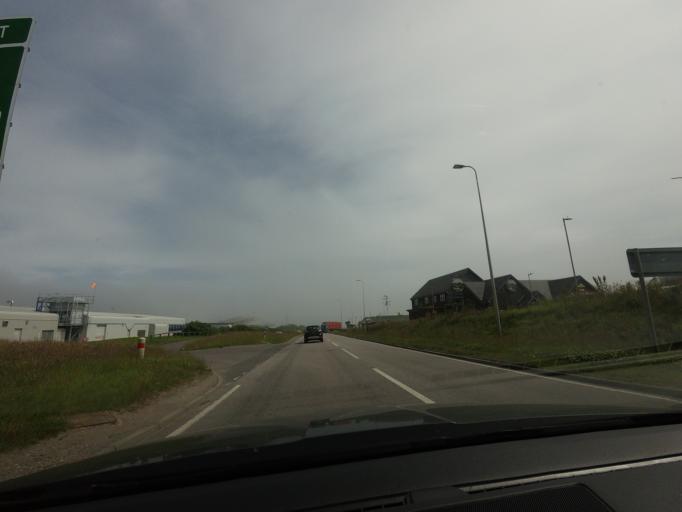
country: GB
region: Scotland
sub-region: Aberdeenshire
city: Peterhead
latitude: 57.4868
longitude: -1.8052
